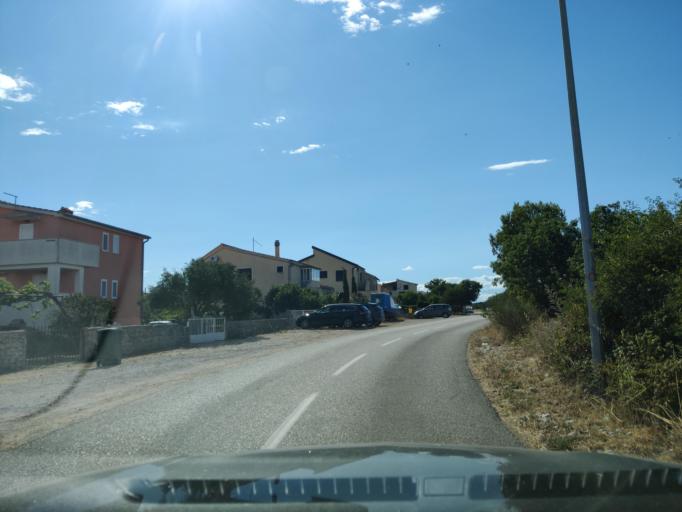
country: HR
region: Sibensko-Kniniska
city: Zaton
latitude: 43.7282
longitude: 15.8415
